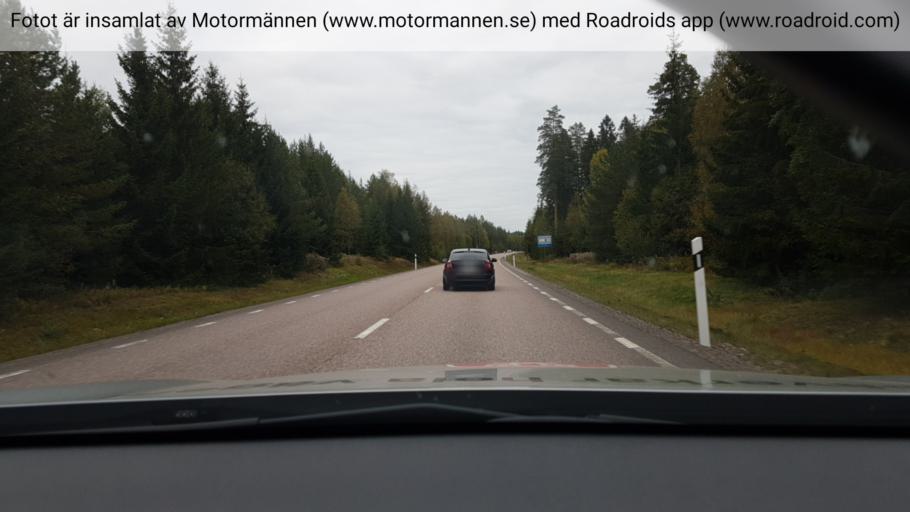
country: SE
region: Gaevleborg
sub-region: Gavle Kommun
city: Hedesunda
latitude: 60.3788
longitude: 16.9656
